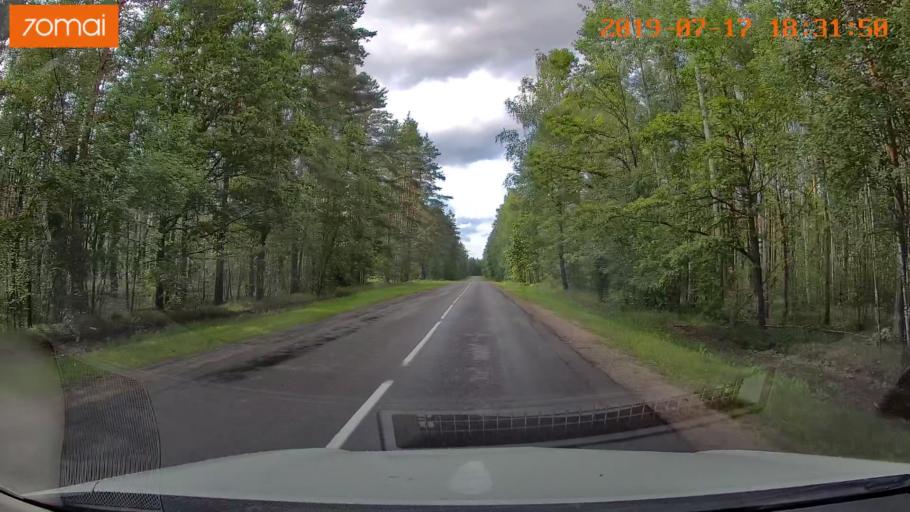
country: BY
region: Mogilev
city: Asipovichy
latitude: 53.2637
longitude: 28.6787
